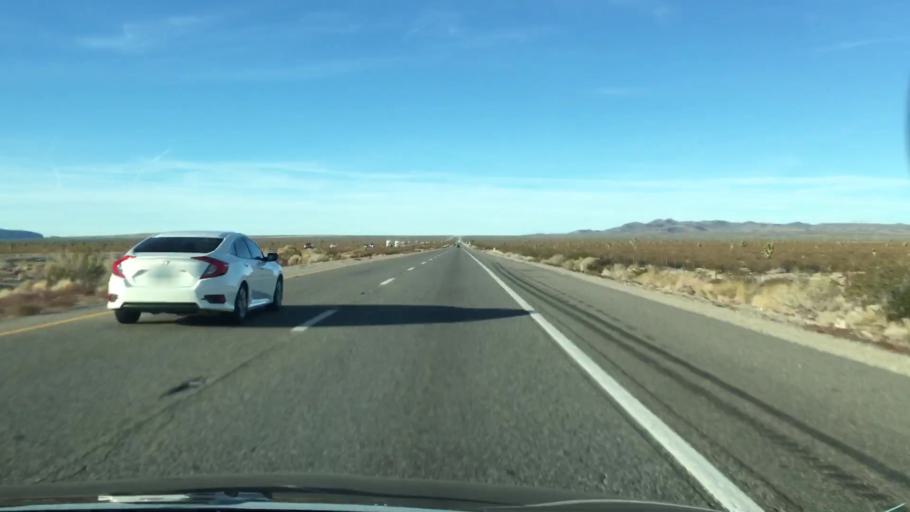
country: US
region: Nevada
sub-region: Clark County
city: Sandy Valley
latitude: 35.4315
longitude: -115.7106
